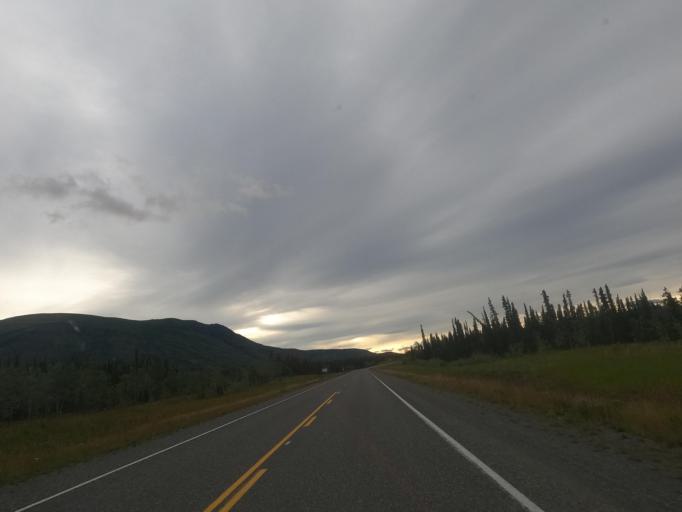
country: CA
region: Yukon
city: Haines Junction
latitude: 60.8539
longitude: -137.0287
